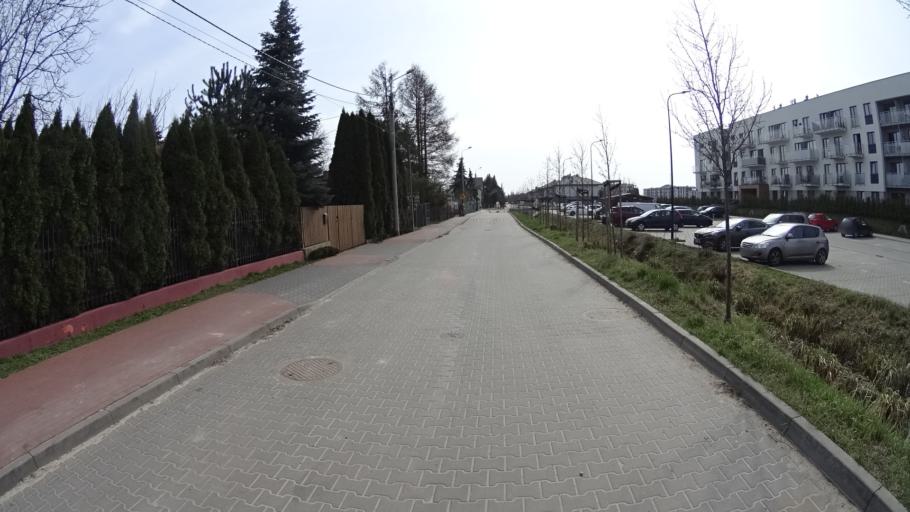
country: PL
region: Masovian Voivodeship
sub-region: Powiat warszawski zachodni
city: Ozarow Mazowiecki
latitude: 52.2185
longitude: 20.7950
